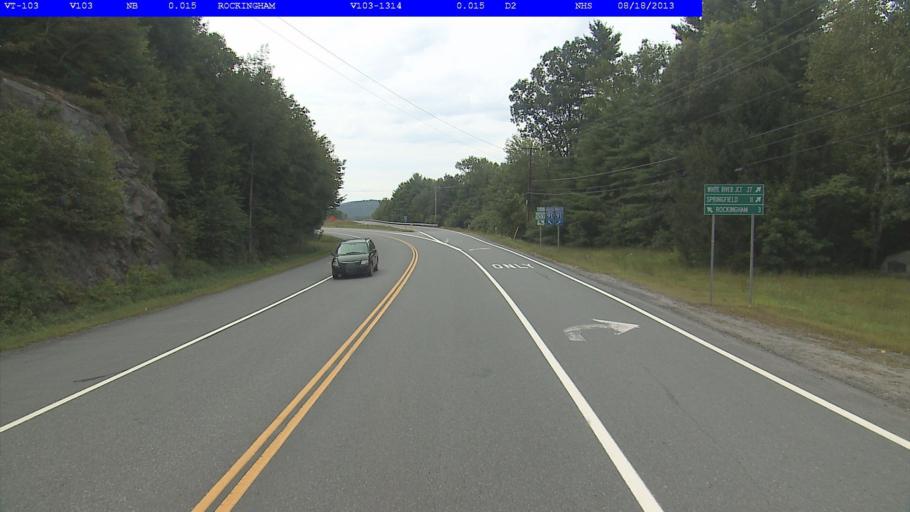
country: US
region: Vermont
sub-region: Windham County
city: Rockingham
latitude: 43.1773
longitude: -72.4601
